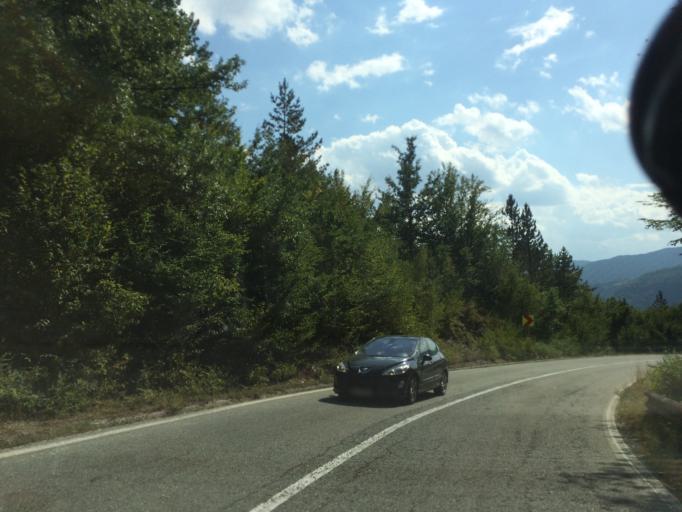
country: ME
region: Opstina Zabljak
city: Zabljak
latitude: 43.1540
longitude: 19.3160
